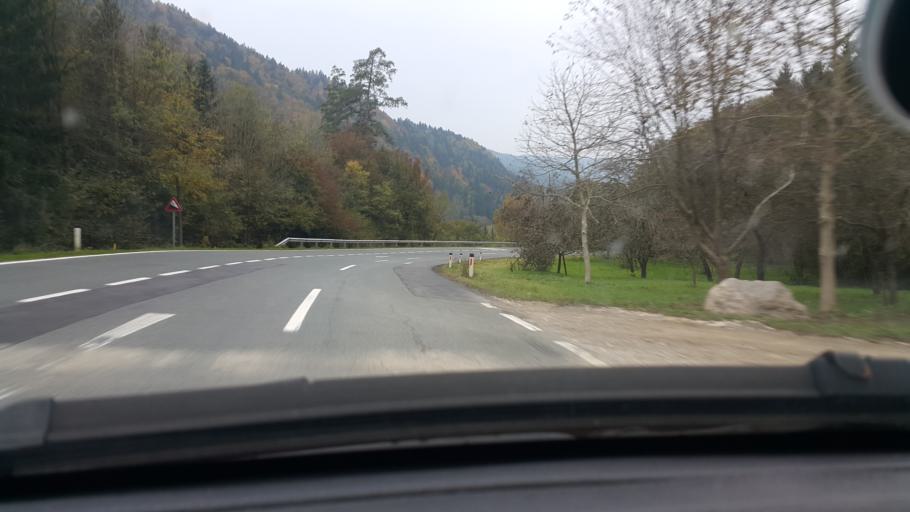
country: AT
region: Carinthia
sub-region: Politischer Bezirk Wolfsberg
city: Lavamund
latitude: 46.6080
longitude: 14.9783
